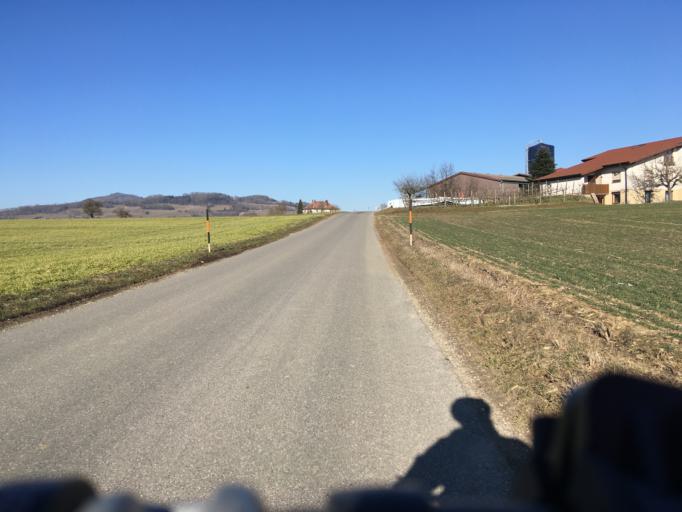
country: DE
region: Baden-Wuerttemberg
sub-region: Freiburg Region
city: Gottmadingen
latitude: 47.7487
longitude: 8.7452
